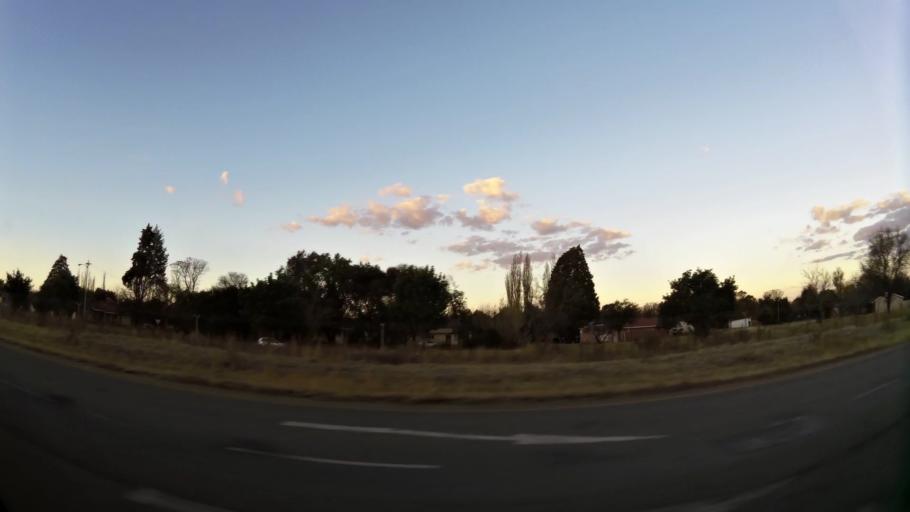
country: ZA
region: North-West
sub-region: Dr Kenneth Kaunda District Municipality
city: Potchefstroom
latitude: -26.6828
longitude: 27.0758
